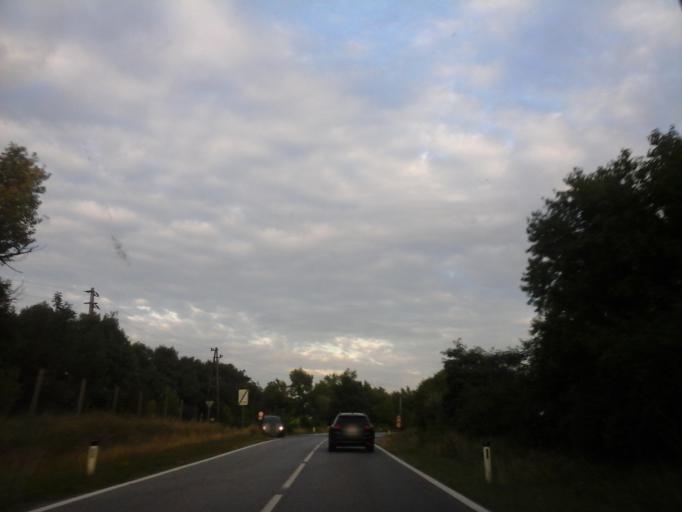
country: AT
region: Lower Austria
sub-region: Politischer Bezirk Wien-Umgebung
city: Rauchenwarth
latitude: 48.1349
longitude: 16.5330
